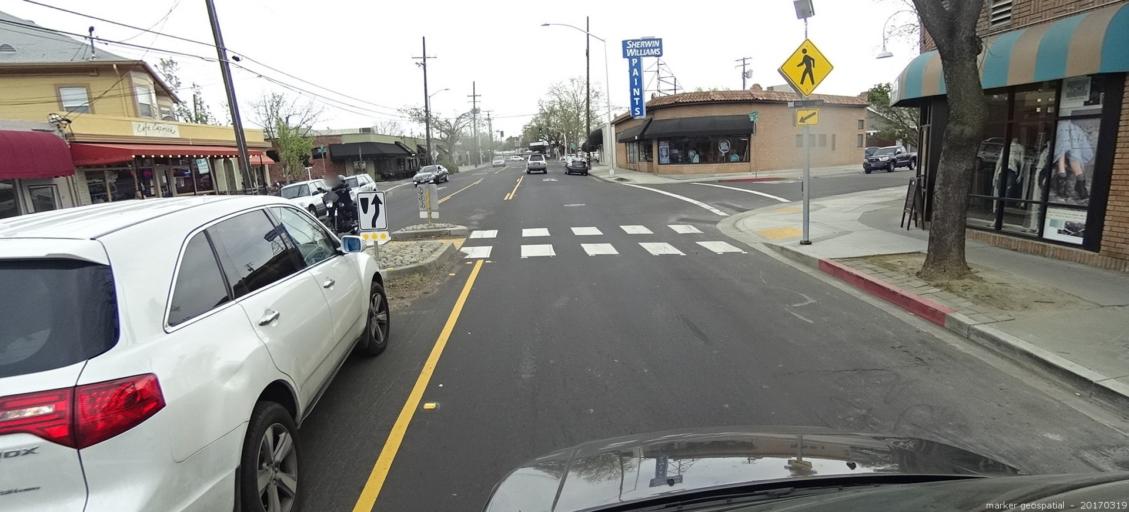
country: US
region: California
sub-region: Sacramento County
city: Sacramento
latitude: 38.5678
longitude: -121.4646
